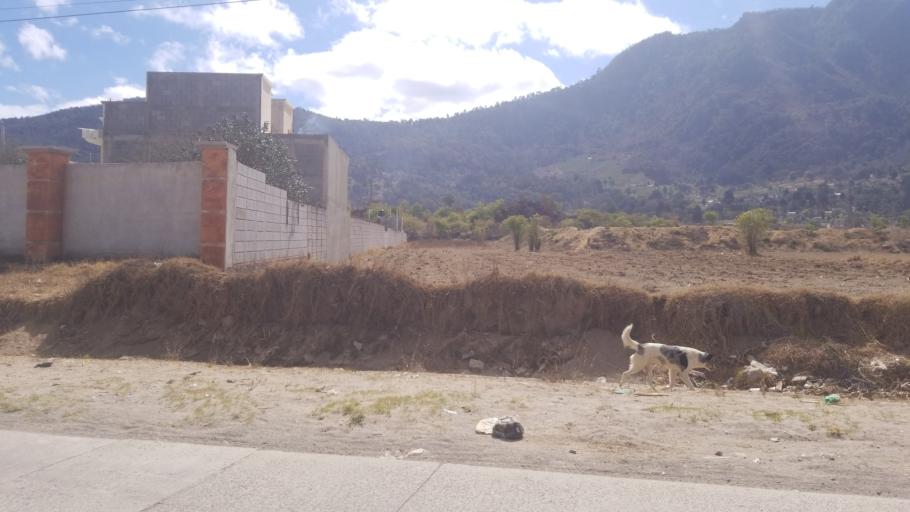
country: GT
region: Quetzaltenango
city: Quetzaltenango
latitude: 14.8078
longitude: -91.5406
